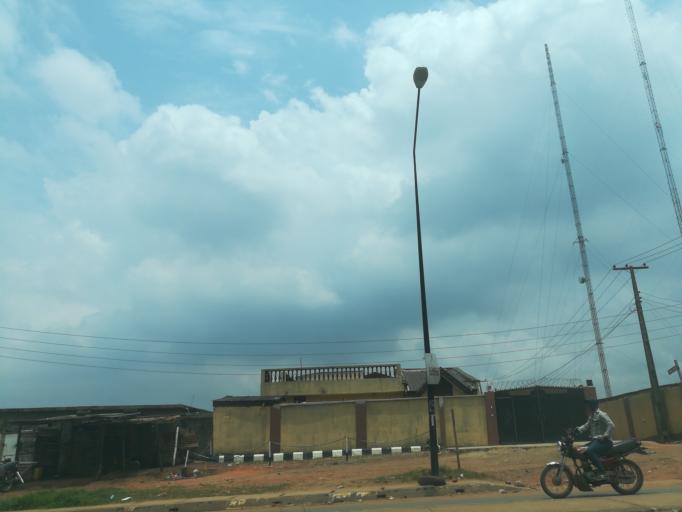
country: NG
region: Lagos
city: Ikorodu
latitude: 6.6268
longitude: 3.5287
